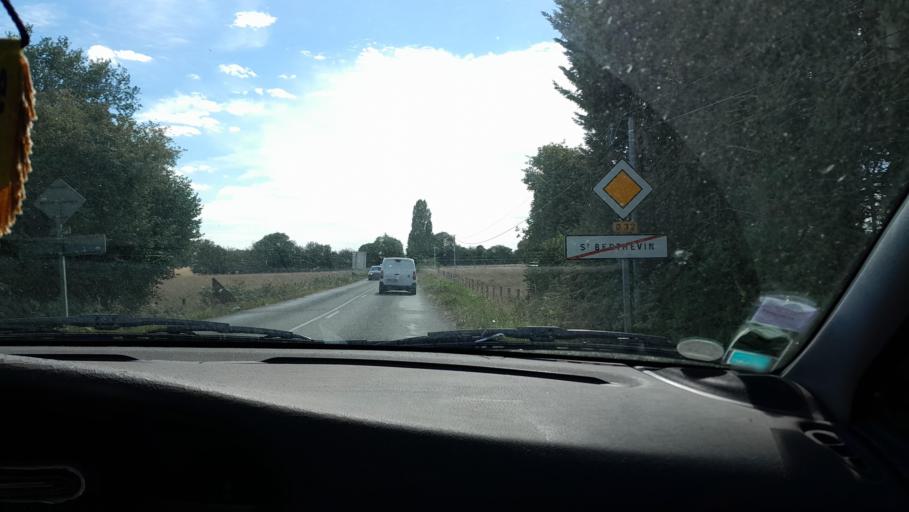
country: FR
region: Pays de la Loire
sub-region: Departement de la Mayenne
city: Saint-Berthevin
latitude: 48.0610
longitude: -0.8438
